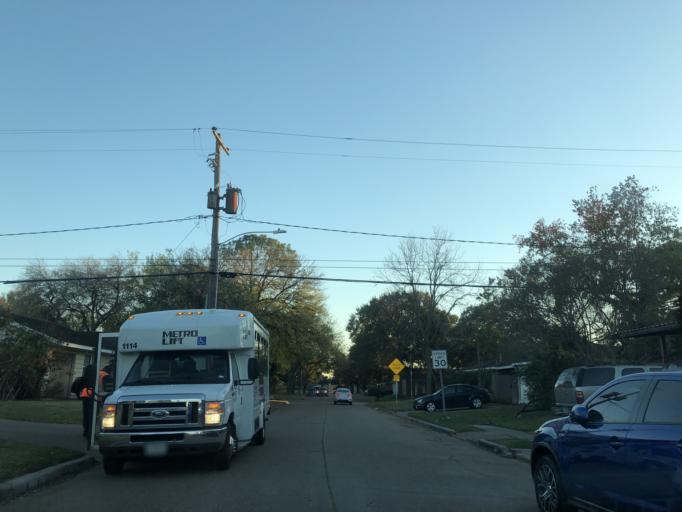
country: US
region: Texas
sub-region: Harris County
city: Bellaire
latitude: 29.6908
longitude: -95.5138
